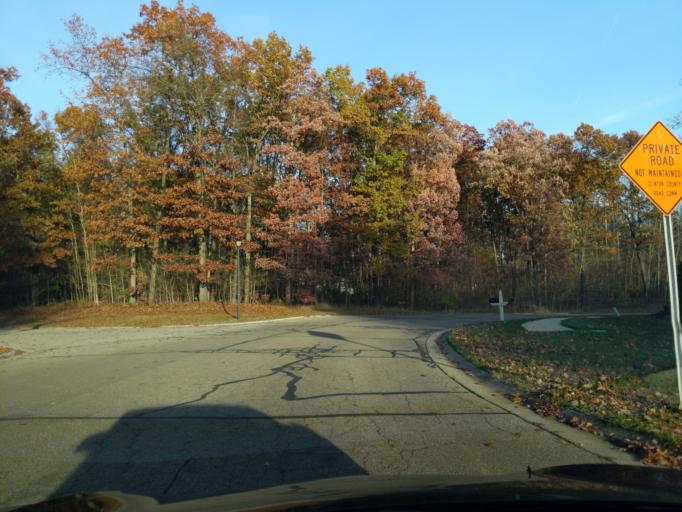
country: US
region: Michigan
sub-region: Clinton County
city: Bath
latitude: 42.7975
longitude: -84.4584
